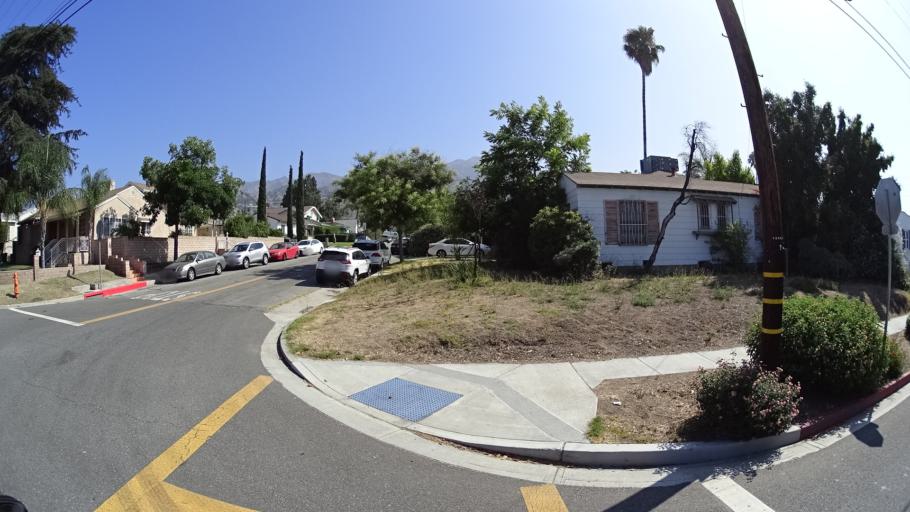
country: US
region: California
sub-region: Los Angeles County
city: Burbank
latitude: 34.1835
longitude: -118.2953
